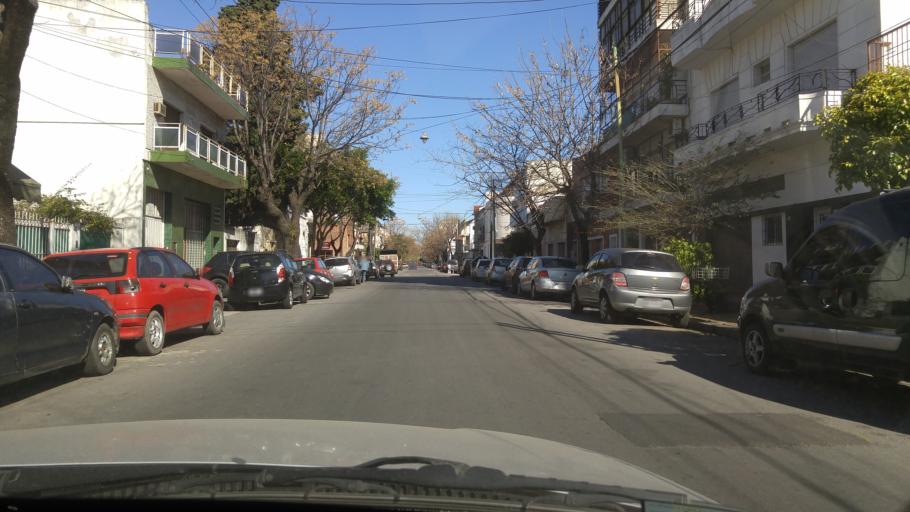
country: AR
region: Buenos Aires F.D.
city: Villa Santa Rita
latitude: -34.6210
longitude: -58.4831
